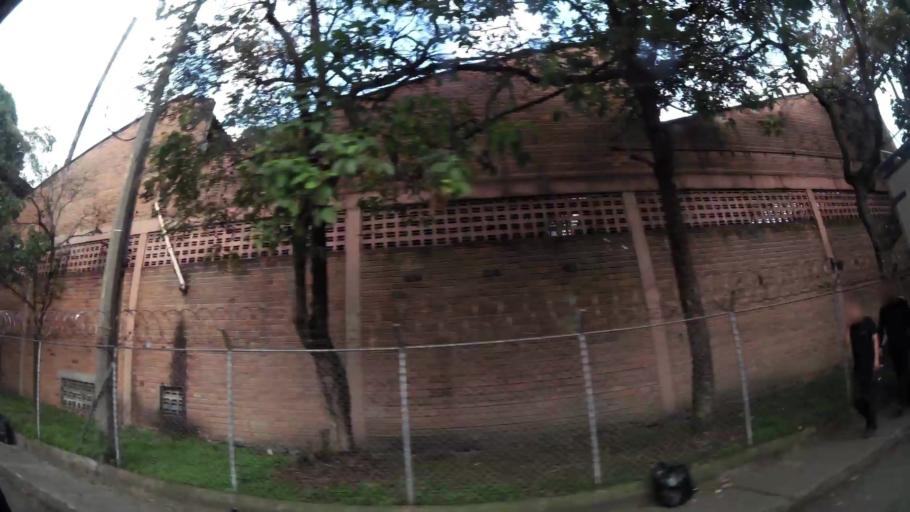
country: CO
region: Antioquia
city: Itagui
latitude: 6.2032
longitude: -75.5832
